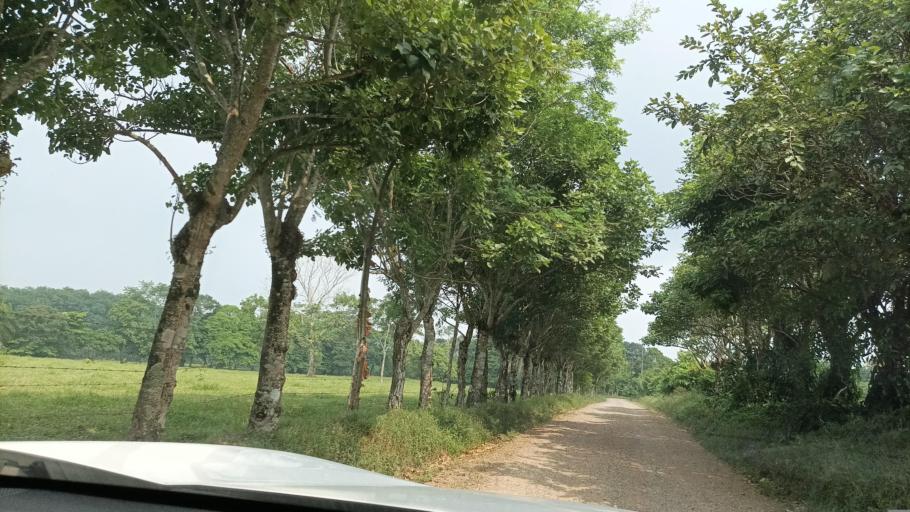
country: MX
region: Veracruz
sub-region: Uxpanapa
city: Poblado 10
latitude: 17.5489
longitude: -94.2255
